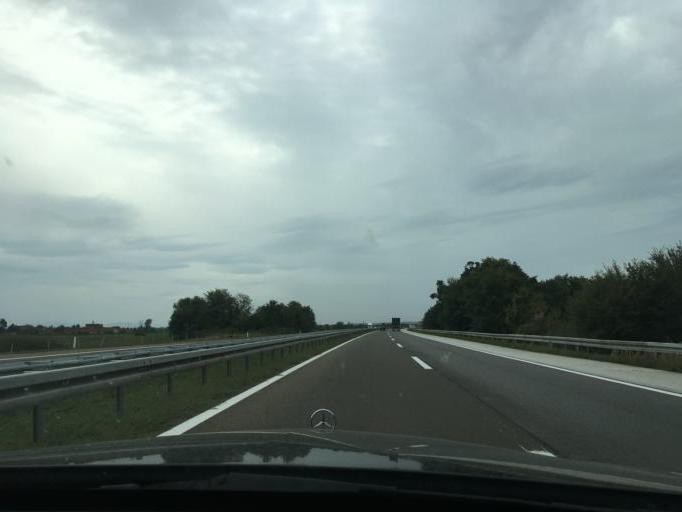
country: RS
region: Central Serbia
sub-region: Pomoravski Okrug
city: Jagodina
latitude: 44.0306
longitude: 21.2633
